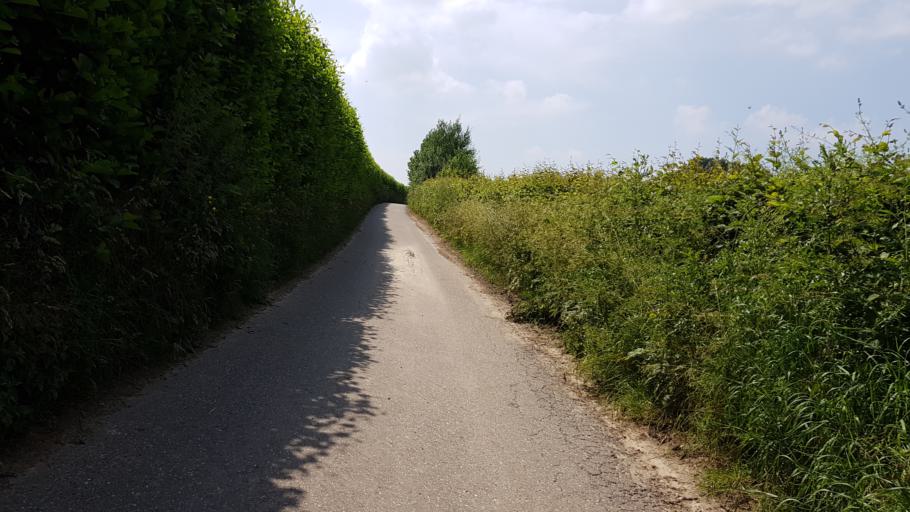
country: NL
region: Limburg
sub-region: Valkenburg aan de Geul
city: Broekhem
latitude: 50.8994
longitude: 5.8151
